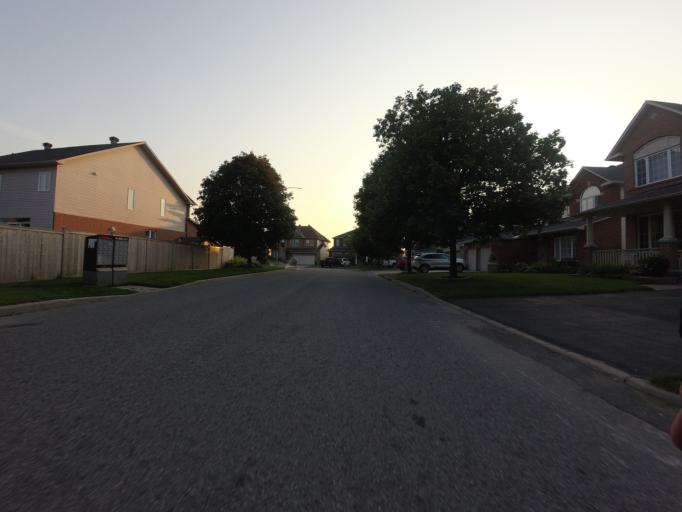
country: CA
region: Ontario
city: Bells Corners
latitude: 45.2837
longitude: -75.8401
